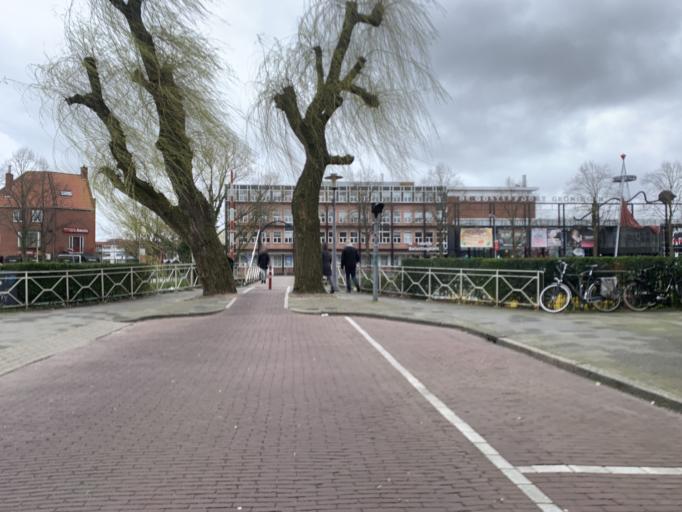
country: NL
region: Groningen
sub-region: Gemeente Groningen
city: Groningen
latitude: 53.2152
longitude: 6.5754
